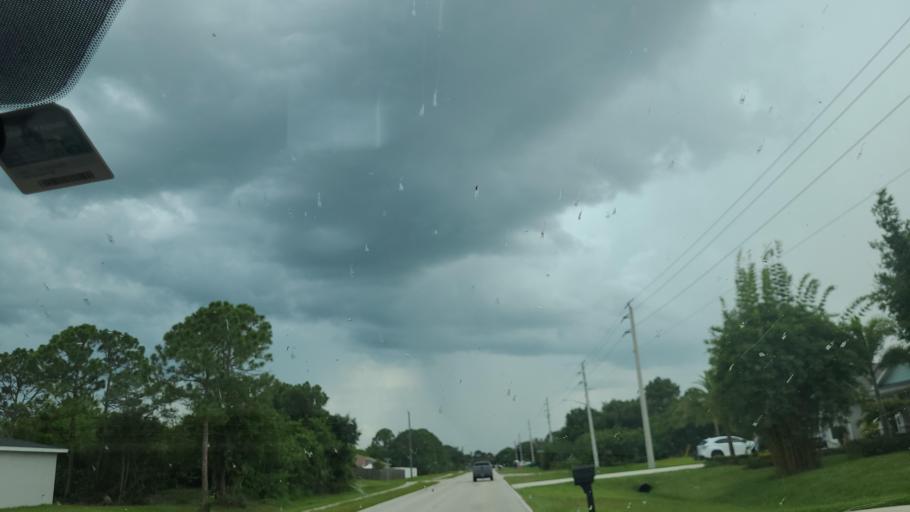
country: US
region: Florida
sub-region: Saint Lucie County
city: Port Saint Lucie
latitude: 27.2133
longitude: -80.3836
